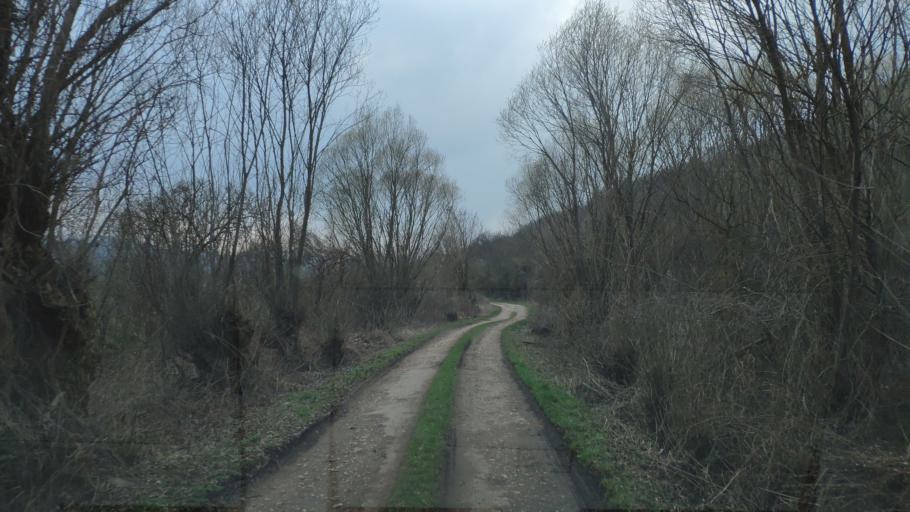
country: SK
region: Kosicky
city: Roznava
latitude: 48.6602
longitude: 20.3822
